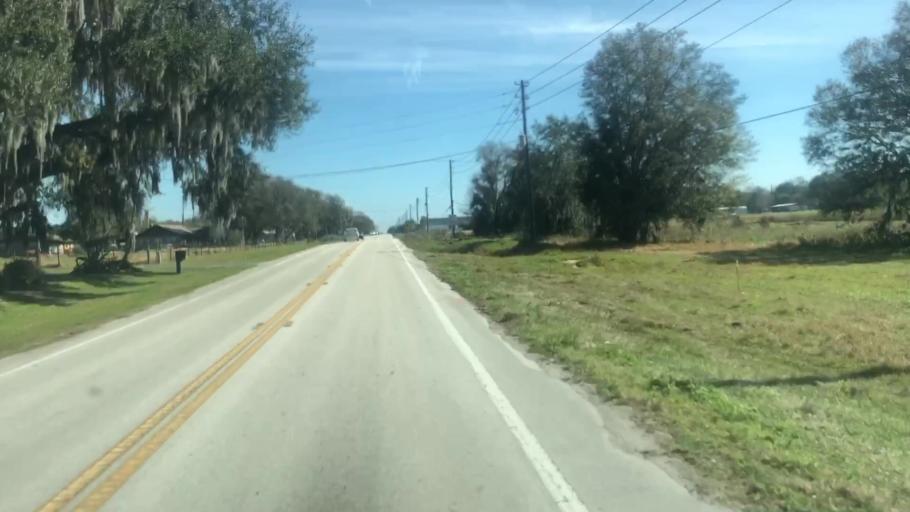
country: US
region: Florida
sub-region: Polk County
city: Winston
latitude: 27.9965
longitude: -82.0511
